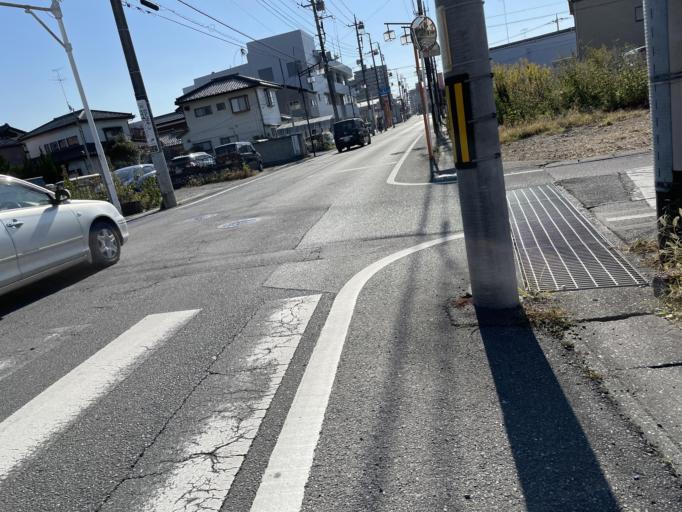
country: JP
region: Gunma
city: Tatebayashi
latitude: 36.2506
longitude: 139.5347
